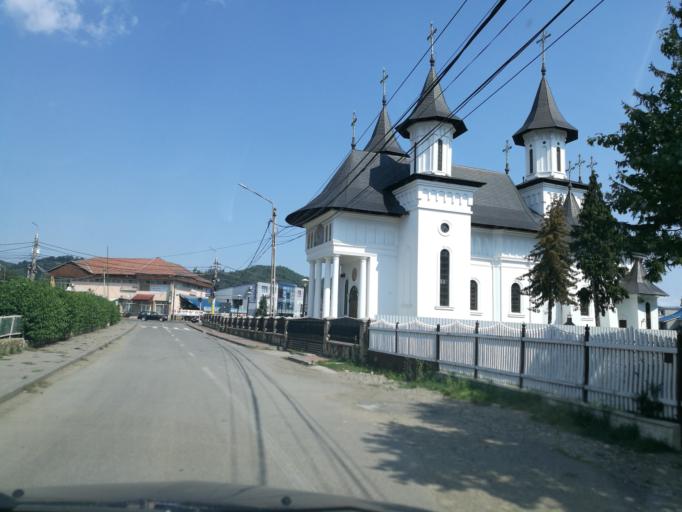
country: RO
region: Neamt
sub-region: Oras Targu Neamt
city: Humulesti
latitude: 47.1981
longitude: 26.3523
